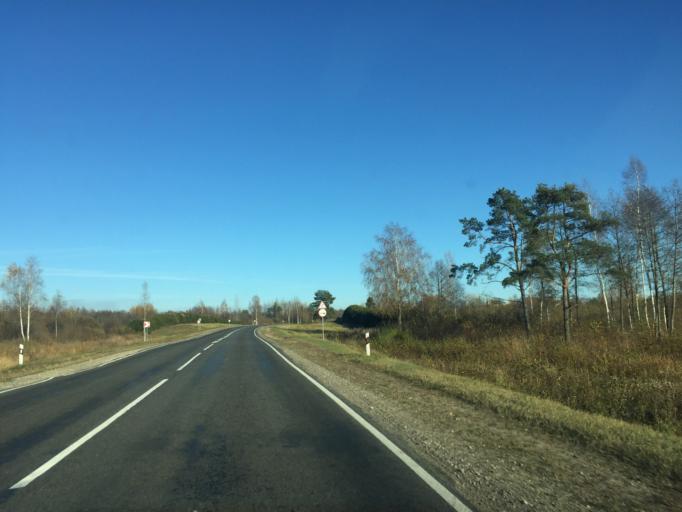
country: BY
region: Vitebsk
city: Dzisna
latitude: 55.3489
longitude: 28.3070
